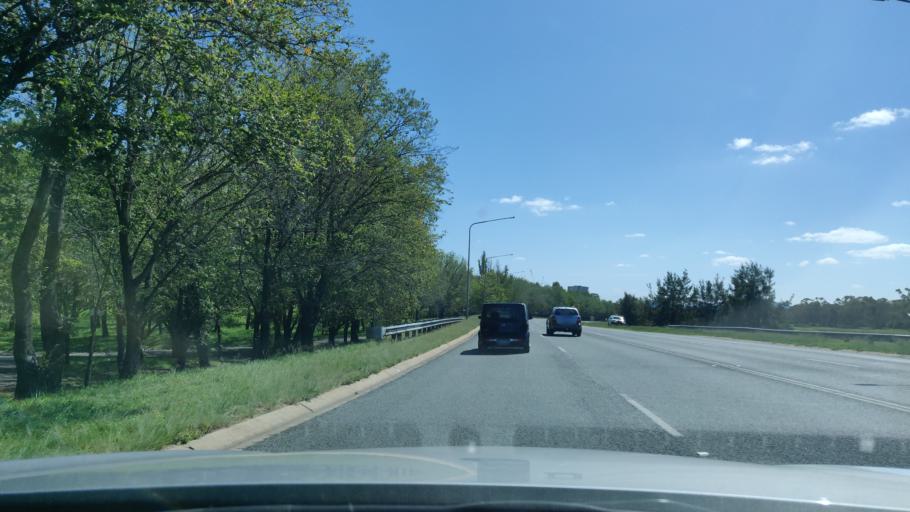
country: AU
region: Australian Capital Territory
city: Macarthur
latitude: -35.3618
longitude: 149.0921
